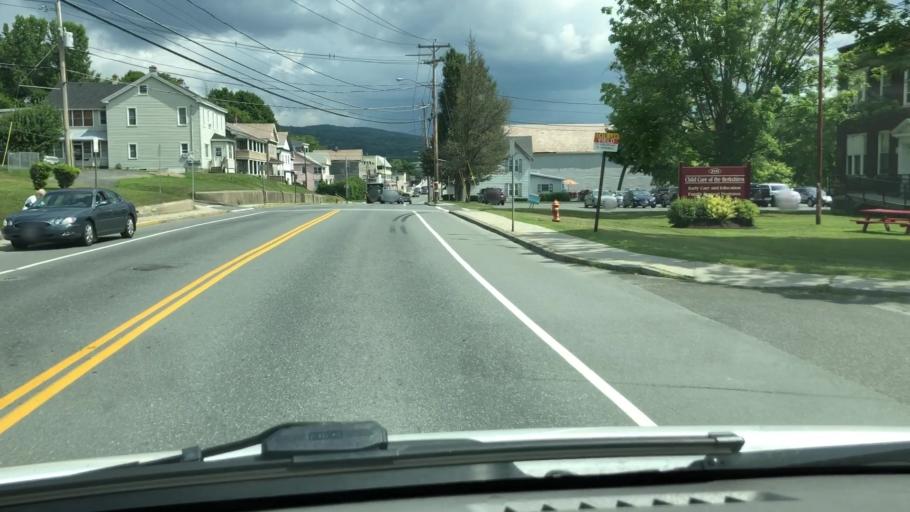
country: US
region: Massachusetts
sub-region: Berkshire County
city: North Adams
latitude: 42.6931
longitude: -73.1147
